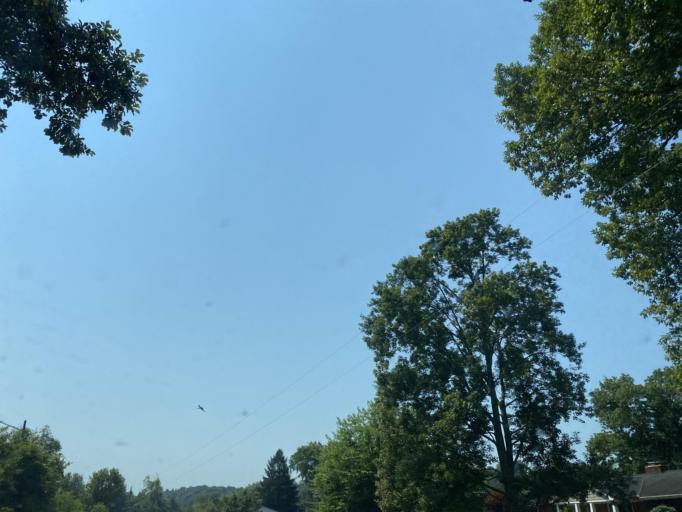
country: US
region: Kentucky
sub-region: Campbell County
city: Claryville
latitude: 38.8283
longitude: -84.4569
